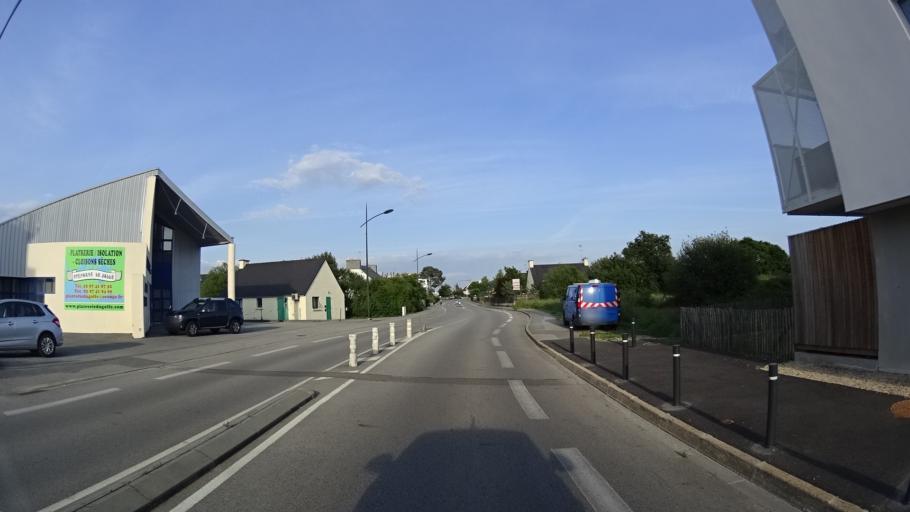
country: FR
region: Brittany
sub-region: Departement du Morbihan
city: Vannes
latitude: 47.6525
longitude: -2.7377
